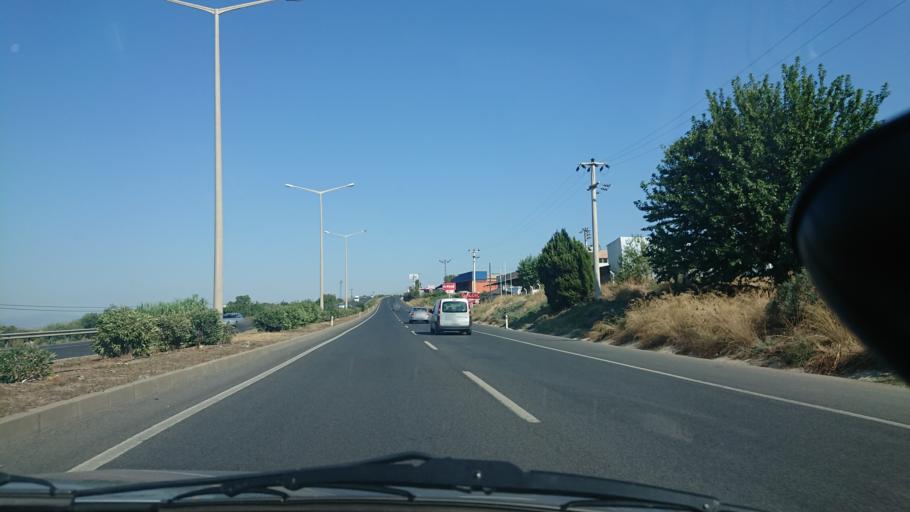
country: TR
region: Manisa
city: Turgutlu
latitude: 38.4953
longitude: 27.7722
